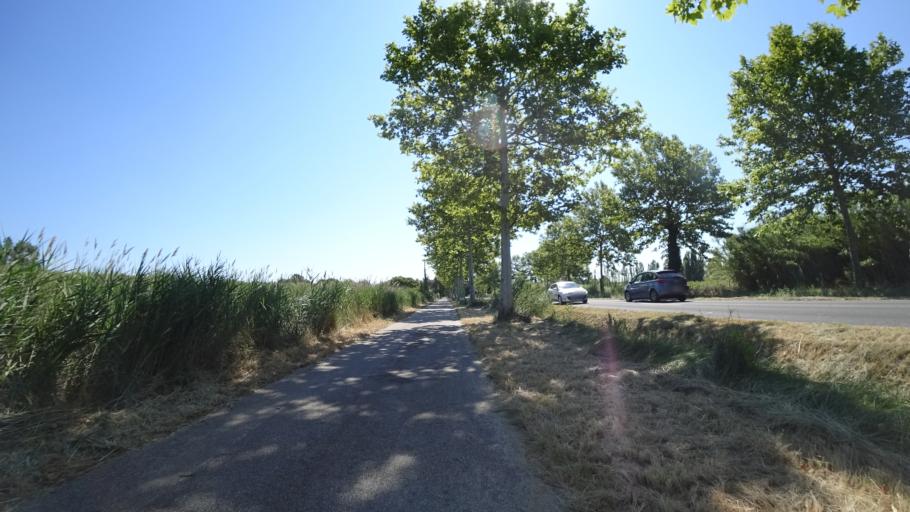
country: FR
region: Languedoc-Roussillon
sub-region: Departement des Pyrenees-Orientales
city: Villelongue-de-la-Salanque
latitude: 42.7272
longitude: 3.0063
